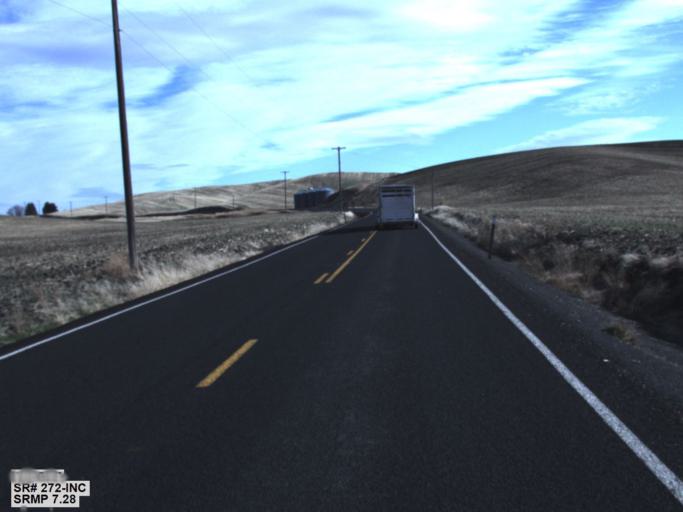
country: US
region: Washington
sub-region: Whitman County
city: Colfax
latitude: 46.9249
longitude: -117.2382
